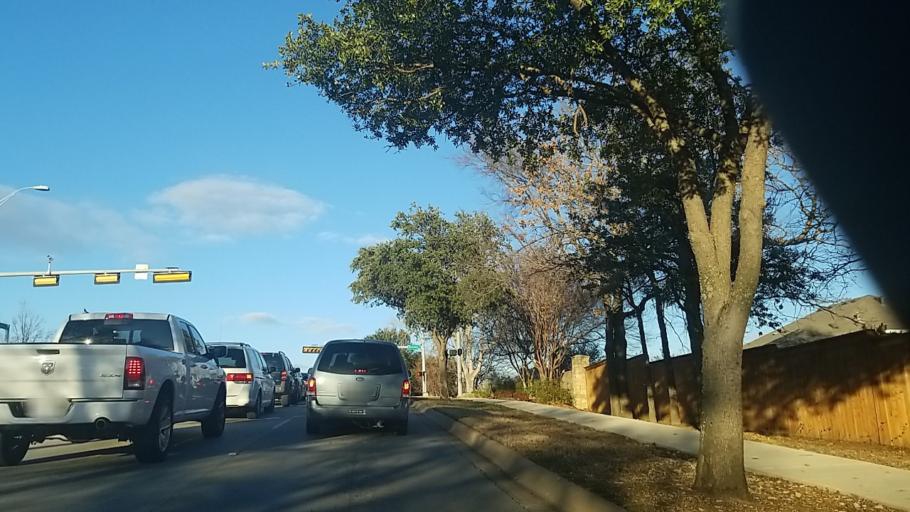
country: US
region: Texas
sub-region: Denton County
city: Denton
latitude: 33.1808
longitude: -97.1105
